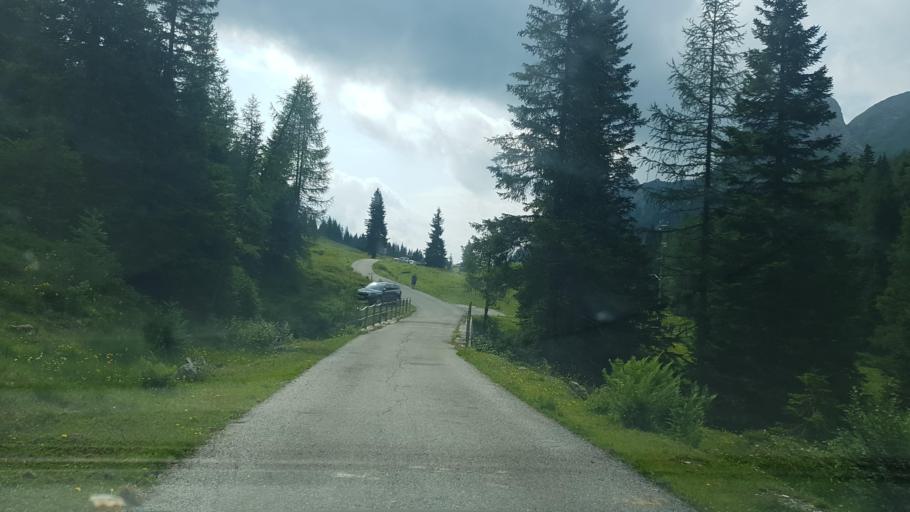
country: IT
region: Friuli Venezia Giulia
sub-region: Provincia di Udine
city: Paularo
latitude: 46.5685
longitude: 13.1682
